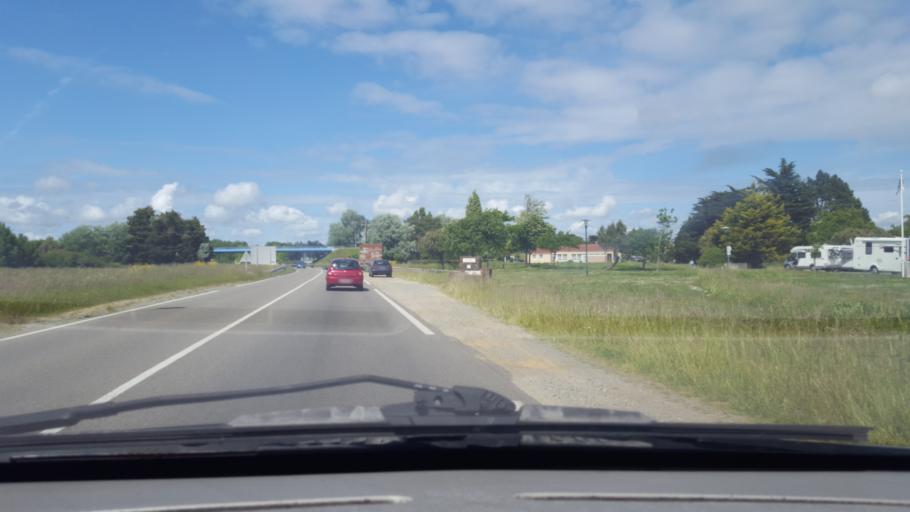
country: FR
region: Pays de la Loire
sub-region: Departement de la Loire-Atlantique
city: Bourgneuf-en-Retz
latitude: 47.0411
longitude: -1.9571
